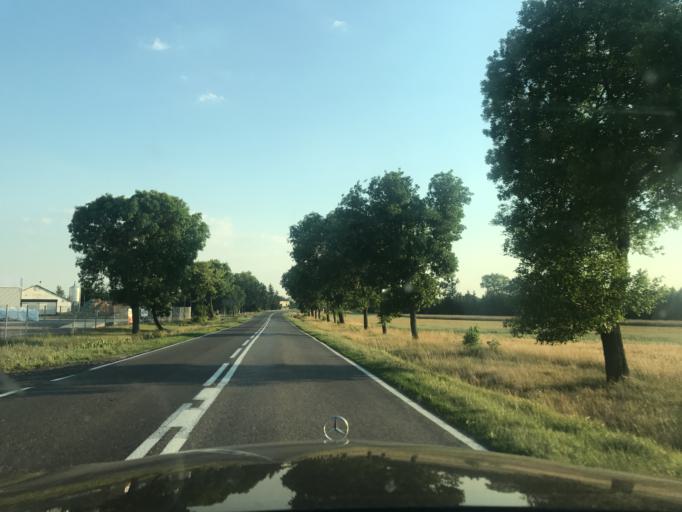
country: PL
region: Lublin Voivodeship
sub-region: Powiat parczewski
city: Debowa Kloda
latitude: 51.6562
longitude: 23.0008
